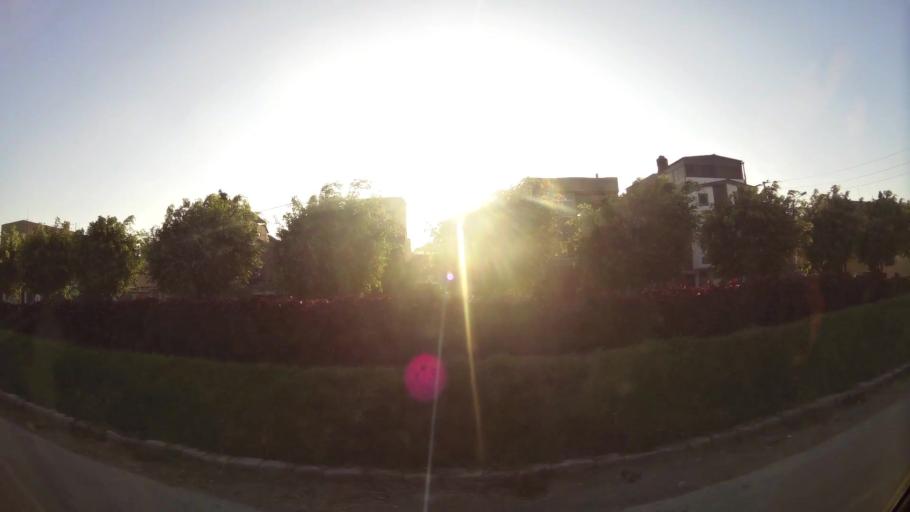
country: PE
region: Lambayeque
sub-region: Provincia de Chiclayo
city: Santa Rosa
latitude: -6.7785
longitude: -79.8301
